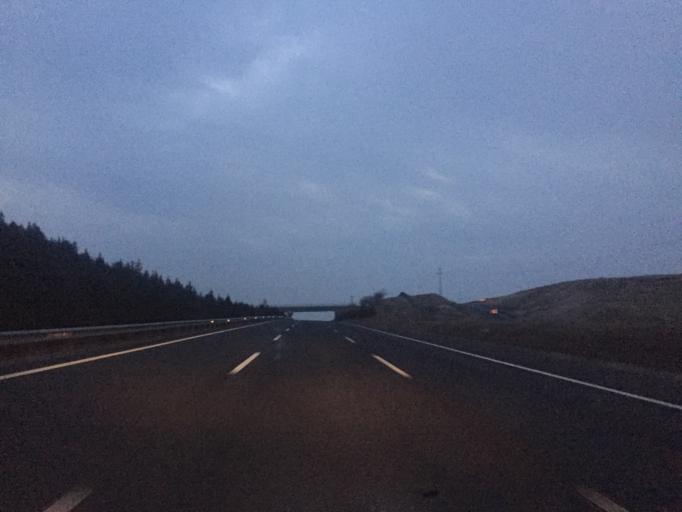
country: TR
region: Sanliurfa
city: Sanliurfa
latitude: 37.1983
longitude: 38.9311
